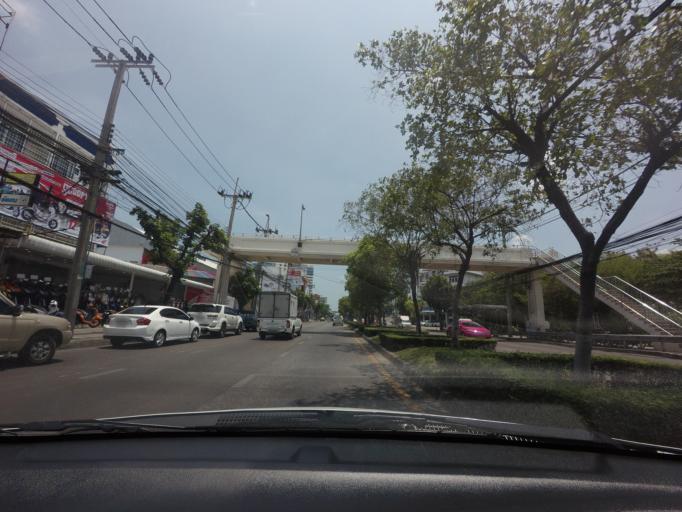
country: TH
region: Bangkok
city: Khan Na Yao
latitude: 13.8282
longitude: 100.6581
